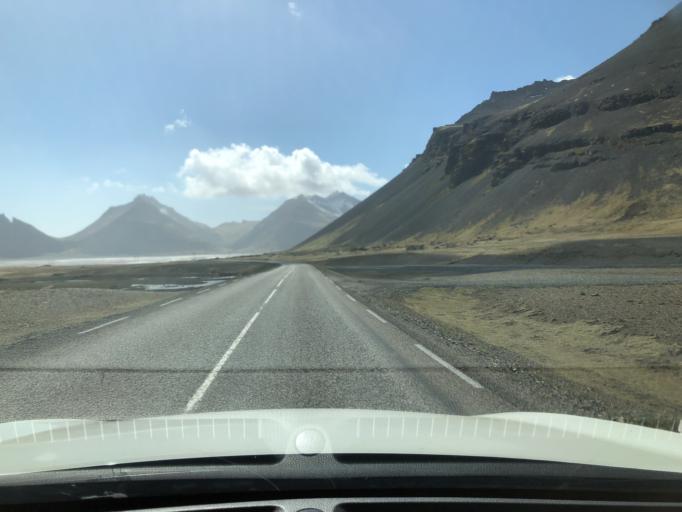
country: IS
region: East
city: Hoefn
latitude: 64.3393
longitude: -14.9296
